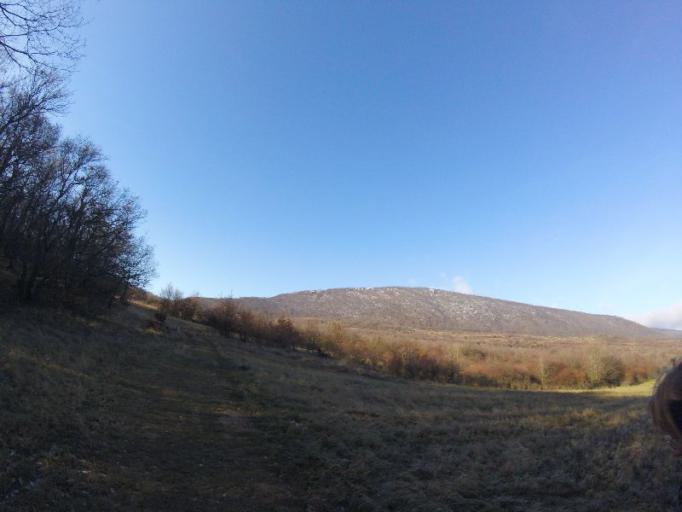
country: HU
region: Pest
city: Pilisszentkereszt
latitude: 47.6858
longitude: 18.8923
